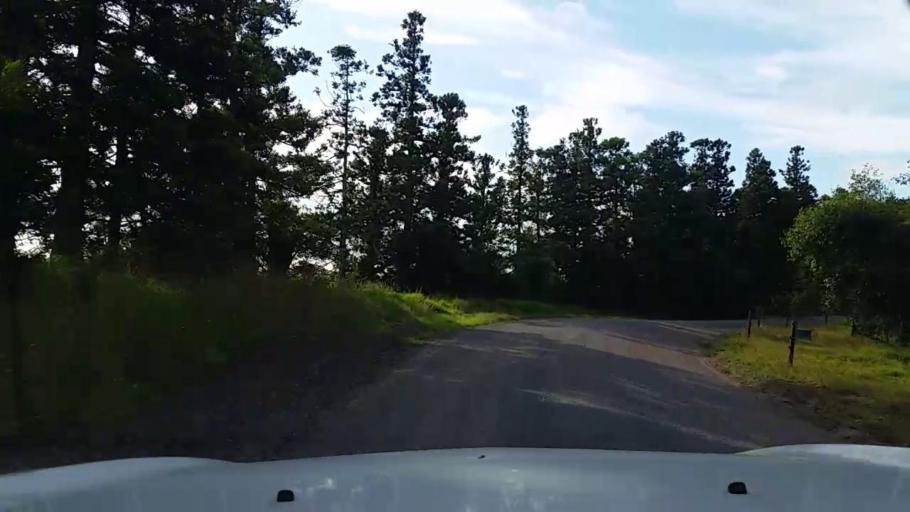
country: NZ
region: Northland
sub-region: Whangarei
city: Maungatapere
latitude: -35.6781
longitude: 174.1784
